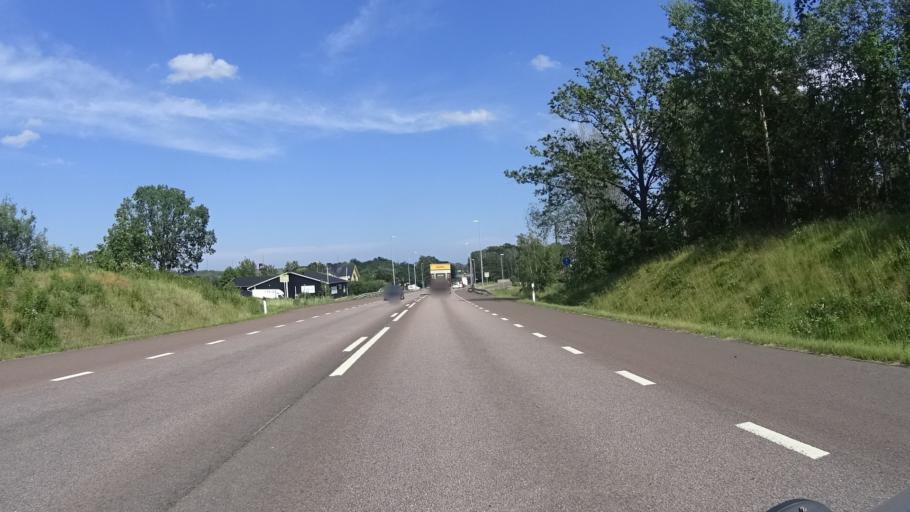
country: SE
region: Kalmar
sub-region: Oskarshamns Kommun
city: Oskarshamn
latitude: 57.2643
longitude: 16.4137
